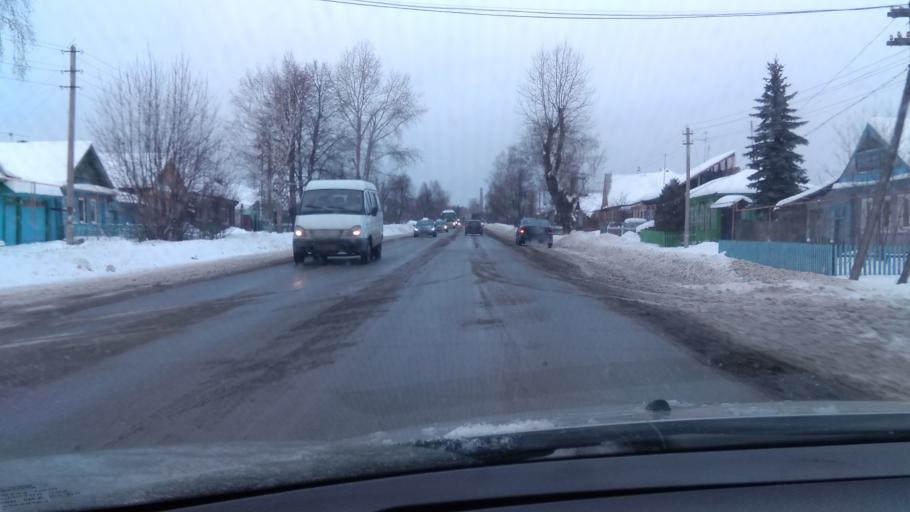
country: RU
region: Sverdlovsk
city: Nikolo-Pavlovskoye
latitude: 57.7889
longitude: 60.0555
